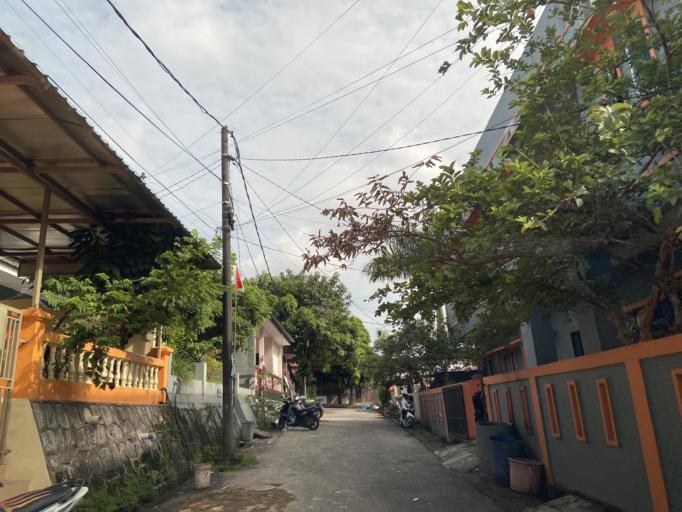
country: SG
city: Singapore
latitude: 1.1318
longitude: 104.0145
